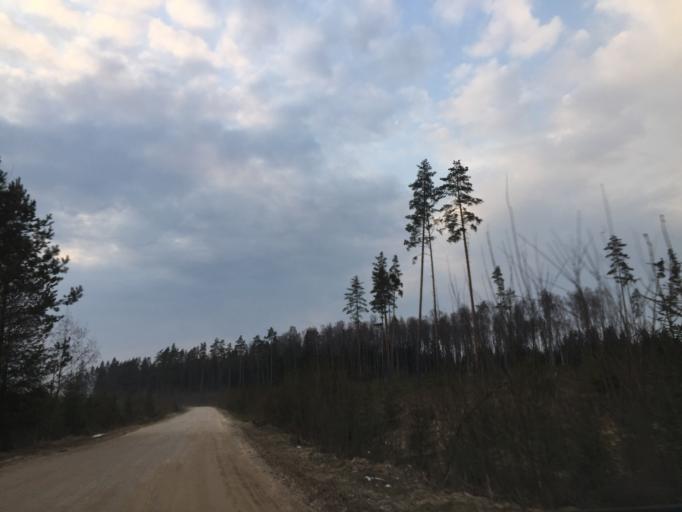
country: LV
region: Raunas
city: Rauna
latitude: 57.1359
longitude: 25.6324
